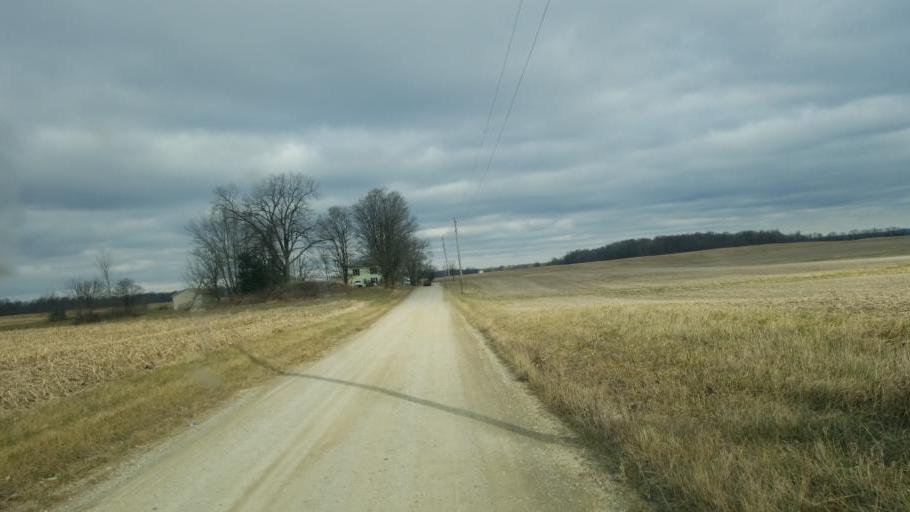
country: US
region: Ohio
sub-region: Richland County
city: Lexington
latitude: 40.5808
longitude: -82.6762
